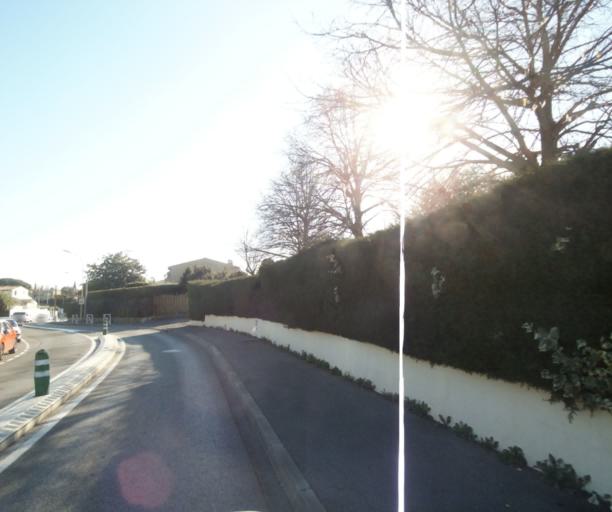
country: FR
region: Provence-Alpes-Cote d'Azur
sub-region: Departement des Alpes-Maritimes
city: Biot
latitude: 43.6049
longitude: 7.1210
